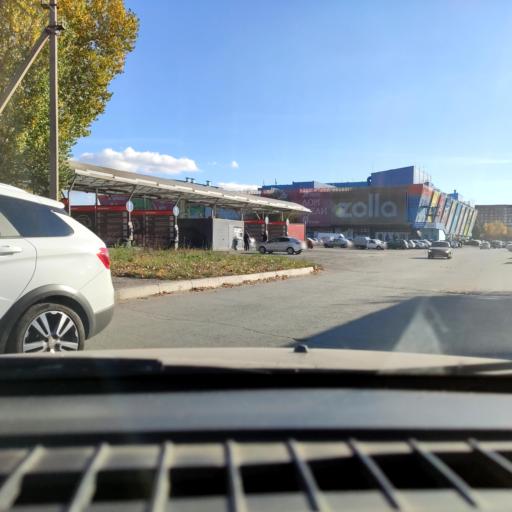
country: RU
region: Samara
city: Tol'yatti
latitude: 53.5201
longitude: 49.2710
